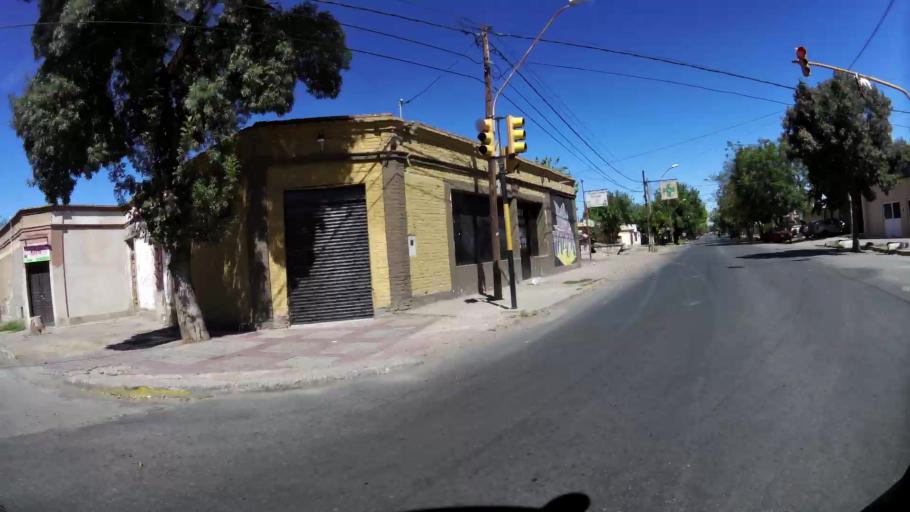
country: AR
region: Mendoza
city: Las Heras
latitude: -32.8325
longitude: -68.8407
